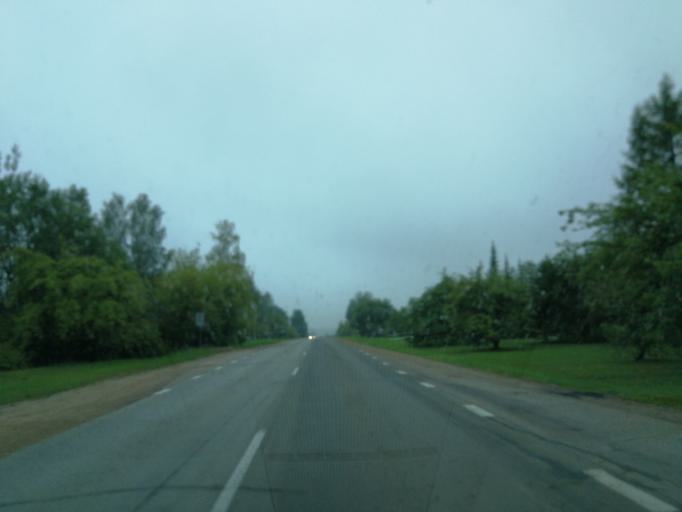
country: LV
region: Preilu Rajons
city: Preili
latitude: 56.2986
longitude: 26.6898
